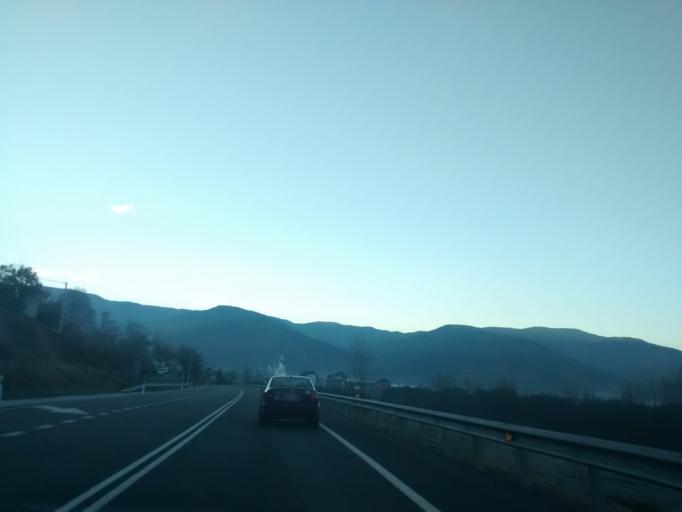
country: ES
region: Catalonia
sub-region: Provincia de Lleida
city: la Seu d'Urgell
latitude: 42.3665
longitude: 1.4548
